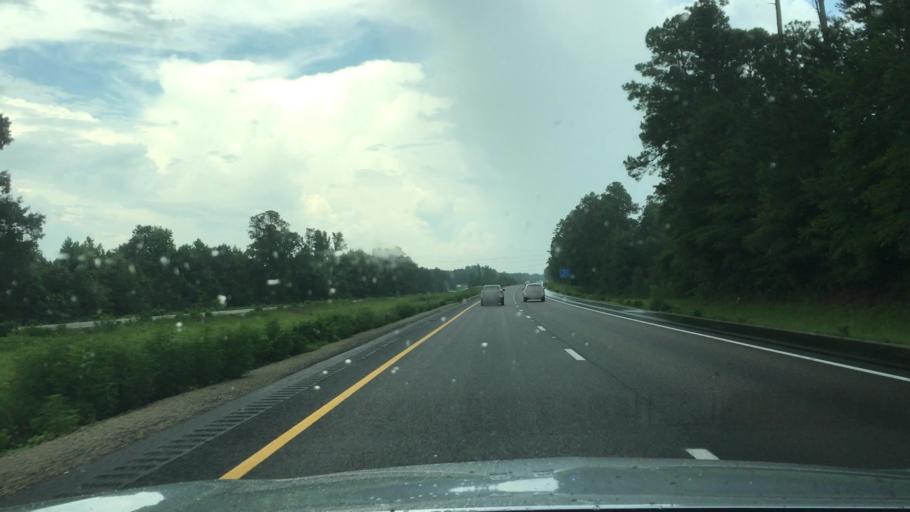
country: US
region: Mississippi
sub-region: Lamar County
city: Purvis
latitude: 31.1894
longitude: -89.3425
